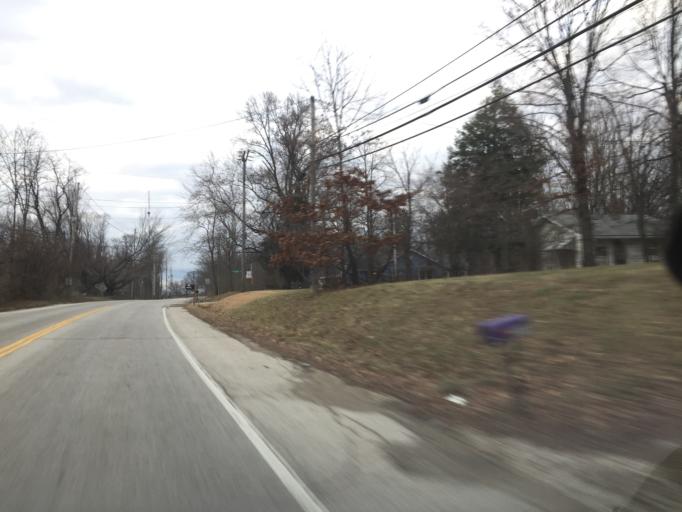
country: US
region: Indiana
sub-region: Monroe County
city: Bloomington
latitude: 39.1881
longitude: -86.5517
